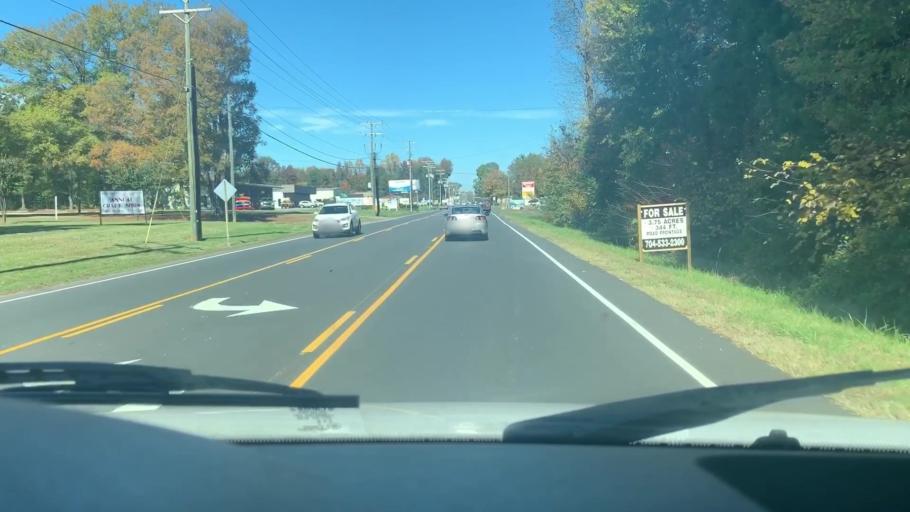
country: US
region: North Carolina
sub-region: Lincoln County
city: Lowesville
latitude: 35.4573
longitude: -80.9922
